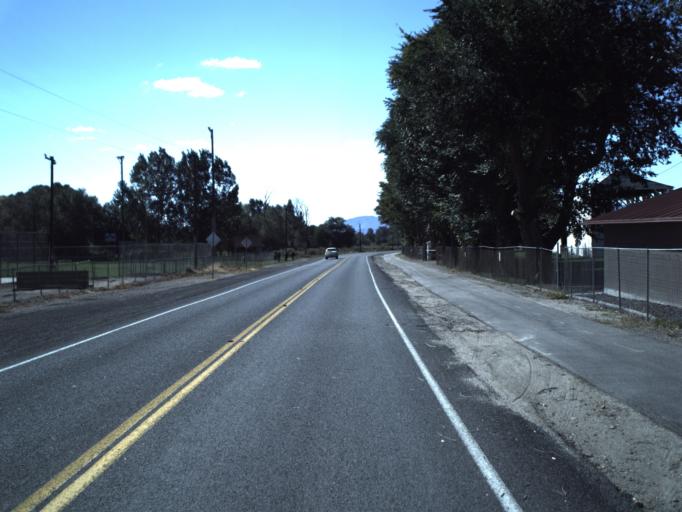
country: US
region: Utah
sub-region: Beaver County
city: Beaver
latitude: 38.2771
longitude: -112.6041
